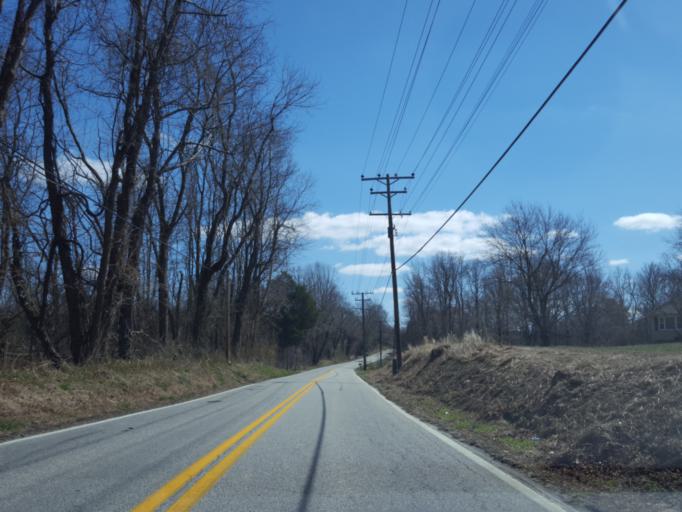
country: US
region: Maryland
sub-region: Calvert County
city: Owings
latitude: 38.7362
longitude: -76.5829
